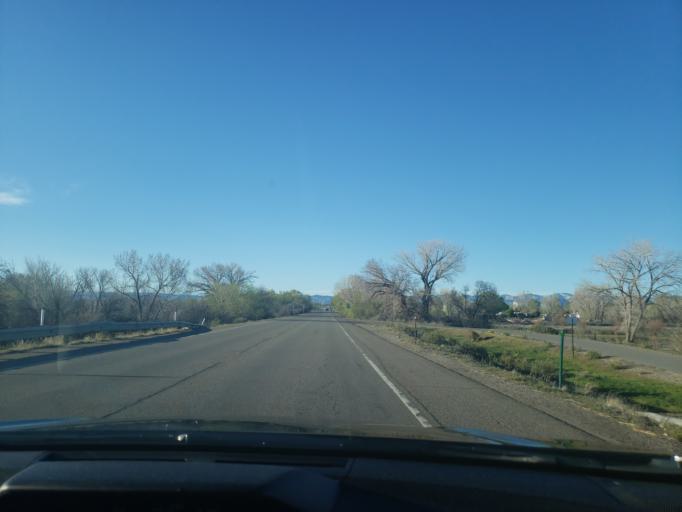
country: US
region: Colorado
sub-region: Mesa County
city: Fruita
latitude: 39.1425
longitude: -108.7382
